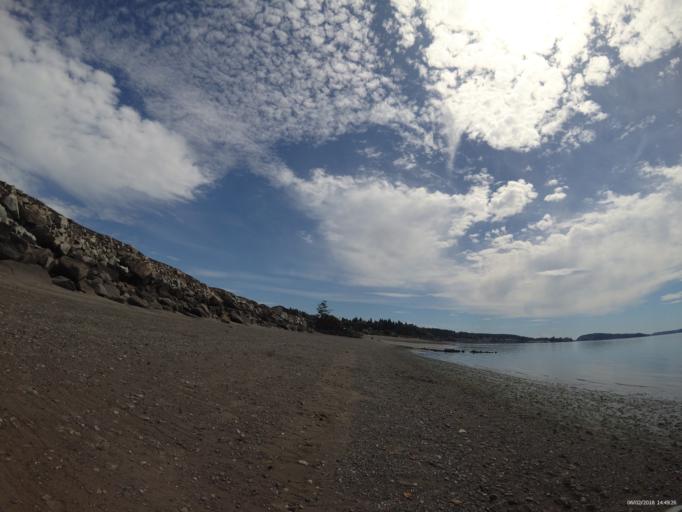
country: US
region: Washington
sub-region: Pierce County
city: Steilacoom
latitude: 47.1946
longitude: -122.5825
